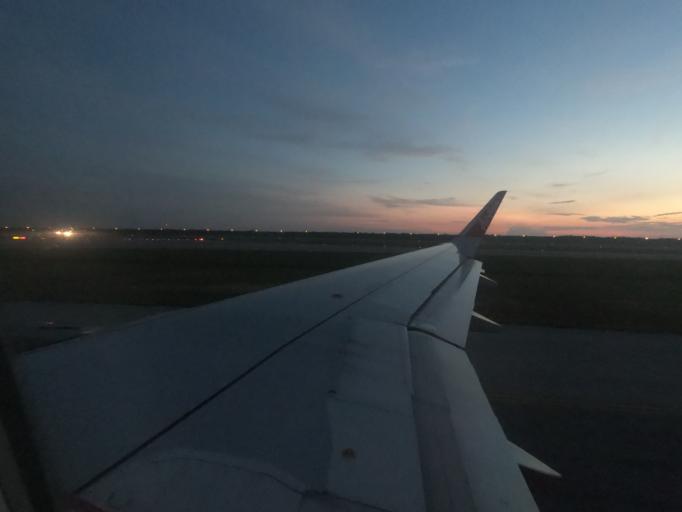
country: MY
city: Sungai Pelek New Village
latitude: 2.7291
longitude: 101.6869
